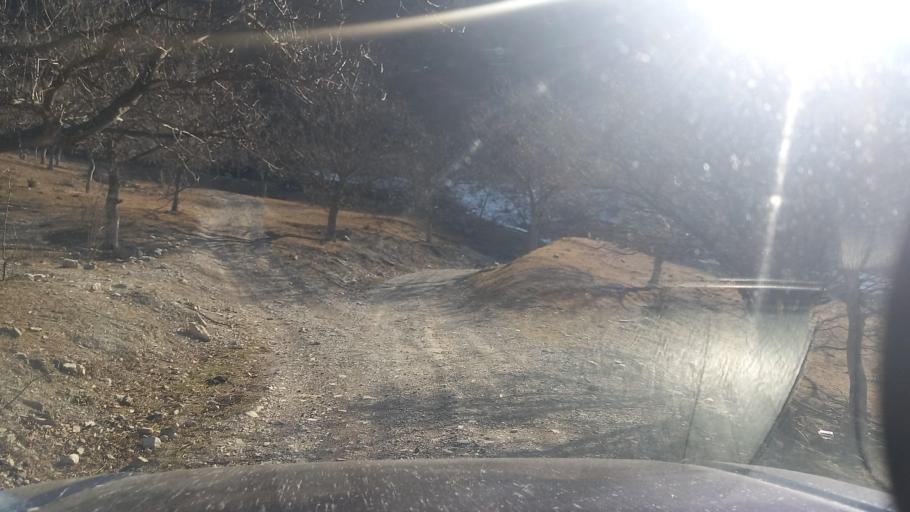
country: RU
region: Ingushetiya
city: Dzhayrakh
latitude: 42.8452
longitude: 44.6629
